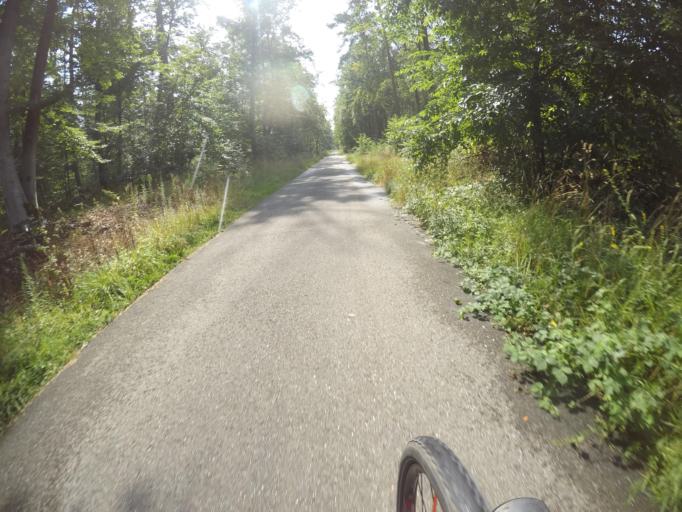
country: DE
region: Baden-Wuerttemberg
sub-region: Karlsruhe Region
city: Reilingen
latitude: 49.3266
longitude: 8.5904
